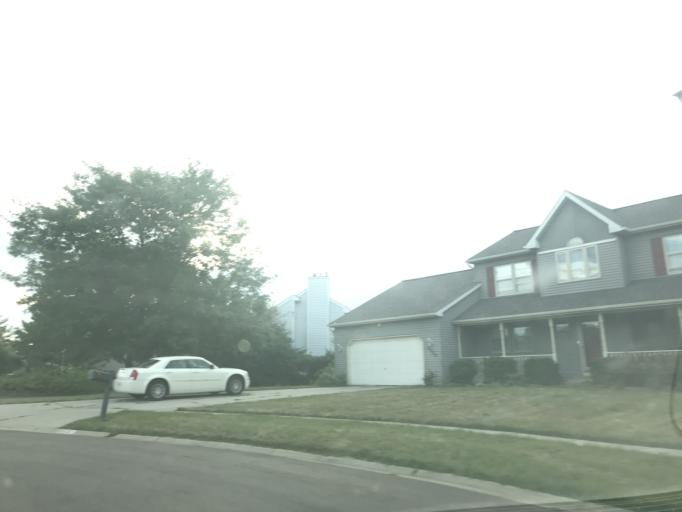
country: US
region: Michigan
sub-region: Eaton County
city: Waverly
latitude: 42.7213
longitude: -84.6185
